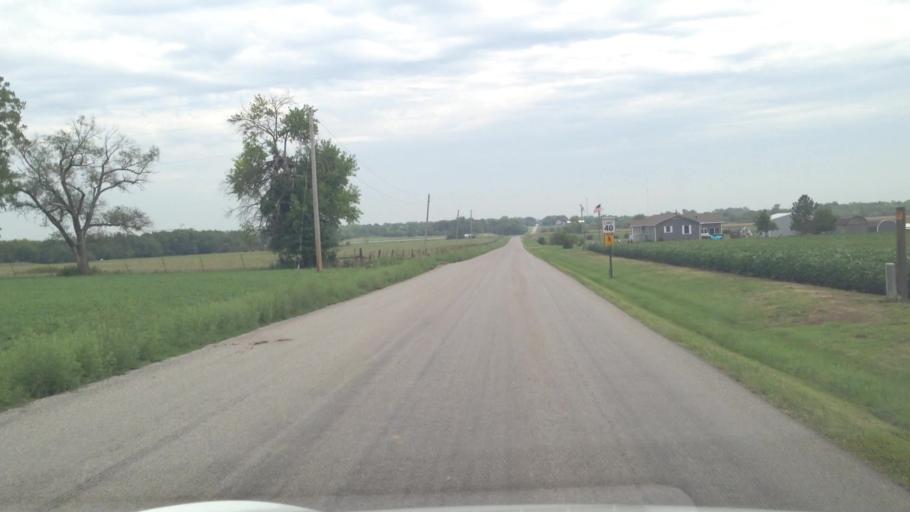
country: US
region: Kansas
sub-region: Crawford County
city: Girard
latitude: 37.4993
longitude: -94.8695
